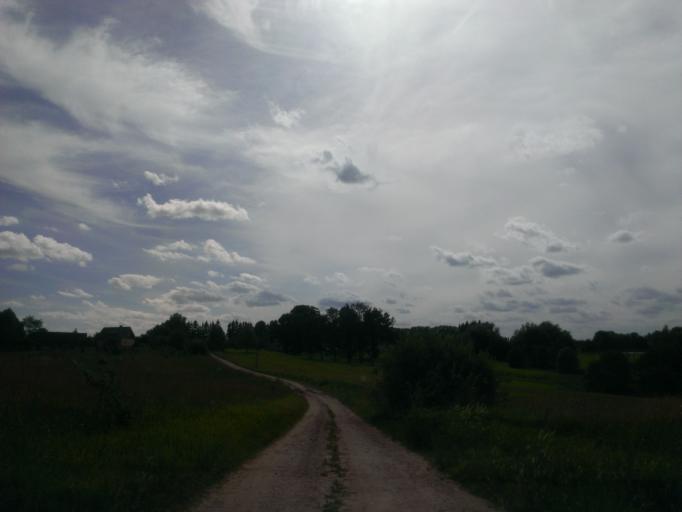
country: LV
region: Ligatne
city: Ligatne
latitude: 57.2265
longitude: 25.0100
